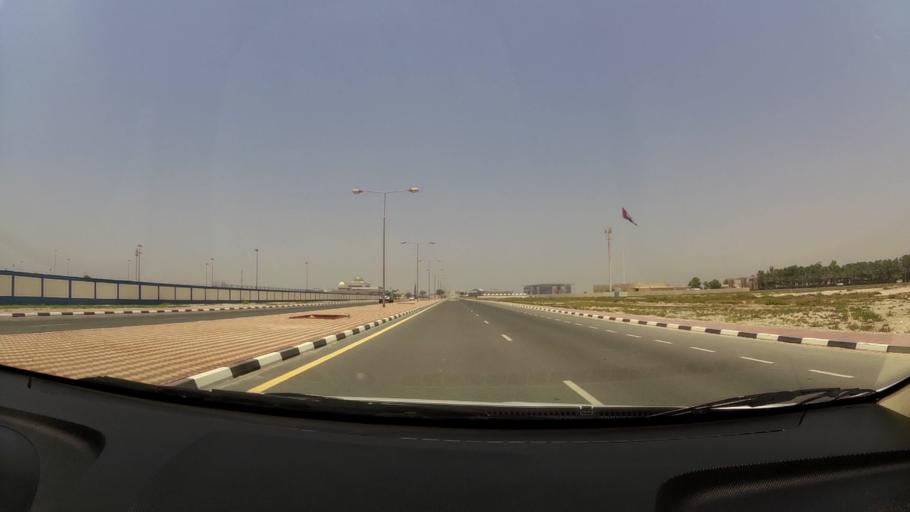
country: AE
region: Umm al Qaywayn
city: Umm al Qaywayn
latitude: 25.5651
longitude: 55.5615
